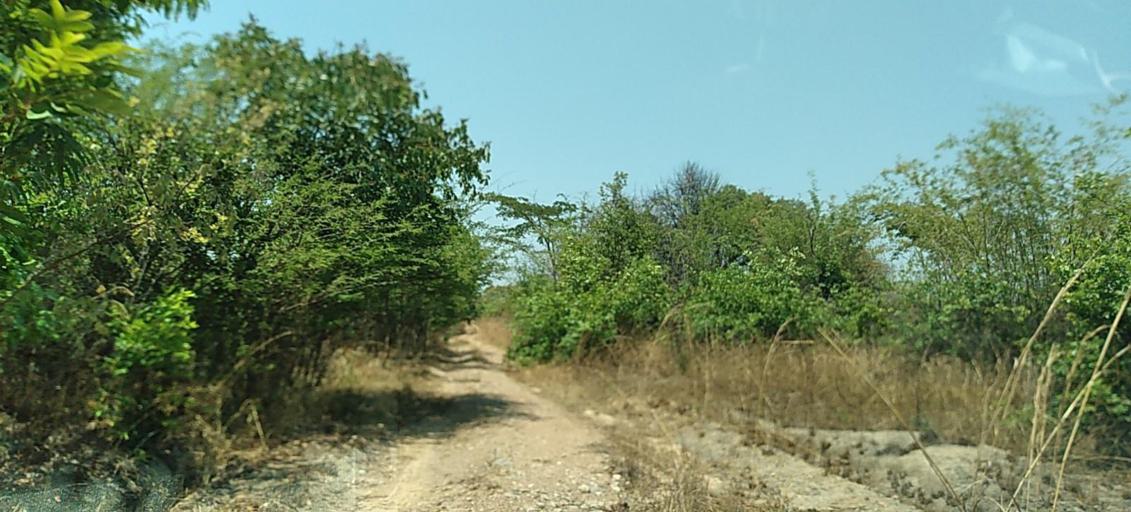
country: ZM
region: Copperbelt
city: Luanshya
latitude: -12.9767
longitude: 28.3298
